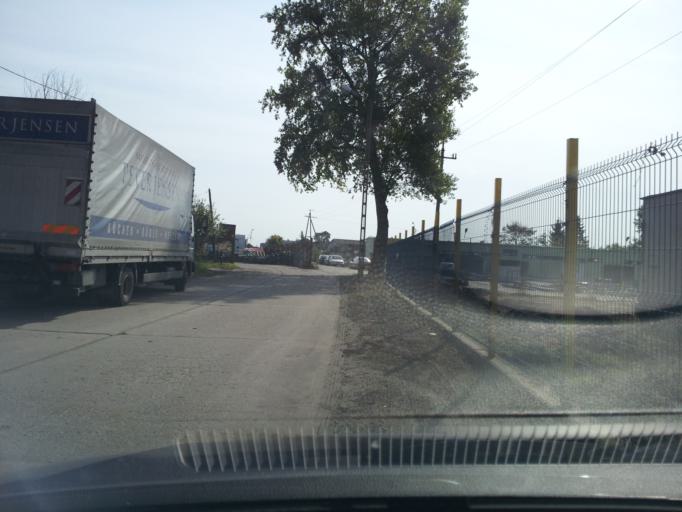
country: PL
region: Kujawsko-Pomorskie
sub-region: Powiat rypinski
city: Rypin
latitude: 53.0646
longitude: 19.4334
